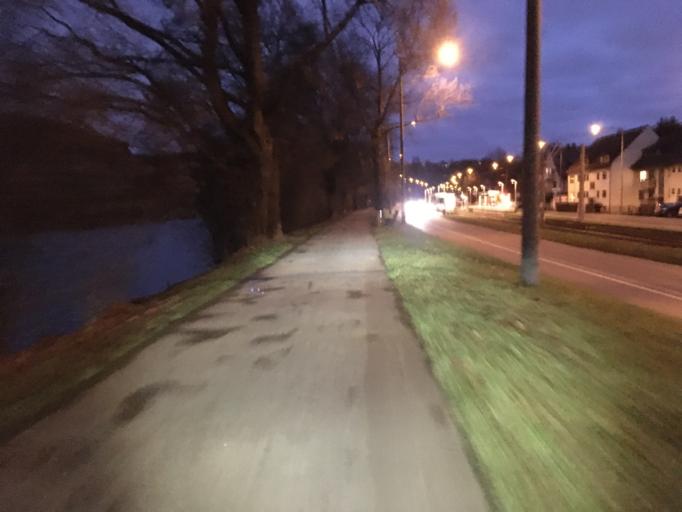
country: DE
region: Baden-Wuerttemberg
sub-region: Regierungsbezirk Stuttgart
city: Stuttgart Muehlhausen
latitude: 48.8250
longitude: 9.2209
